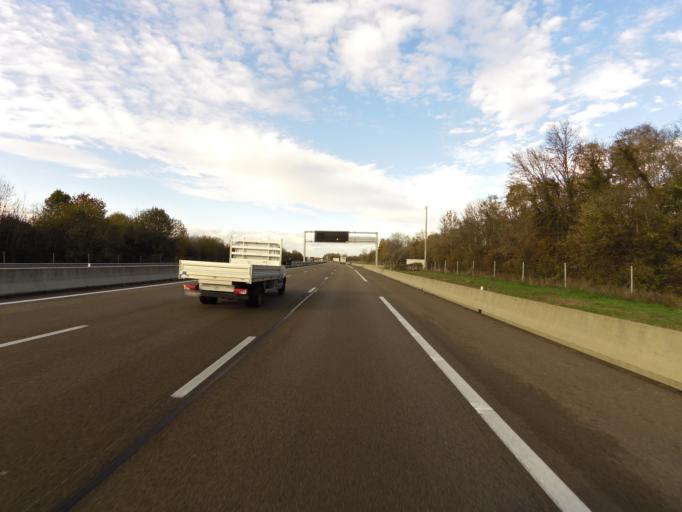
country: FR
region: Bourgogne
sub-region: Departement de la Cote-d'Or
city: Couternon
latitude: 47.3276
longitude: 5.1698
